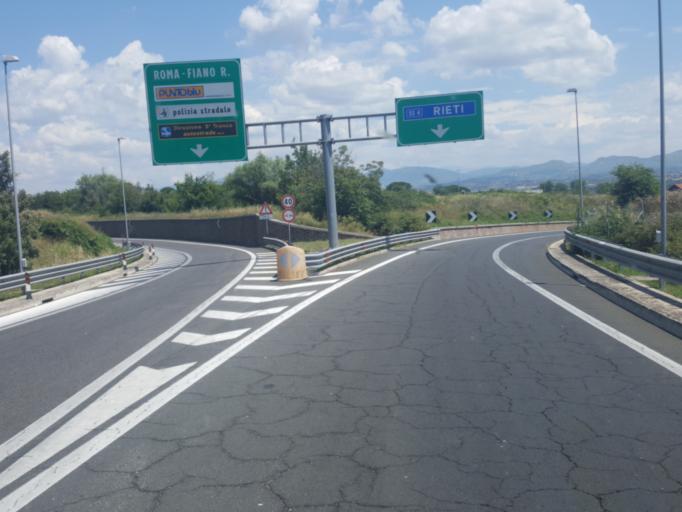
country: IT
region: Latium
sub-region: Citta metropolitana di Roma Capitale
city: Fiano Romano
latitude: 42.1404
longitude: 12.6078
